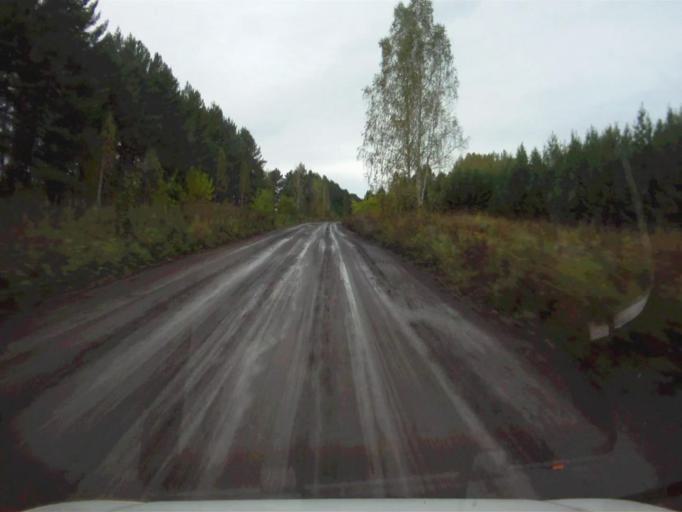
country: RU
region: Chelyabinsk
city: Nyazepetrovsk
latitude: 56.1398
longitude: 59.2966
